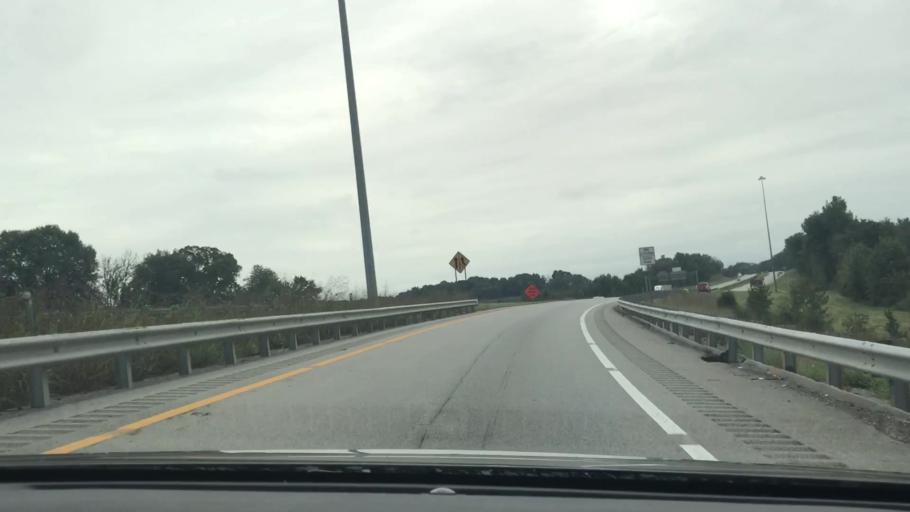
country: US
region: Kentucky
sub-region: Barren County
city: Cave City
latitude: 37.0574
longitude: -86.1107
